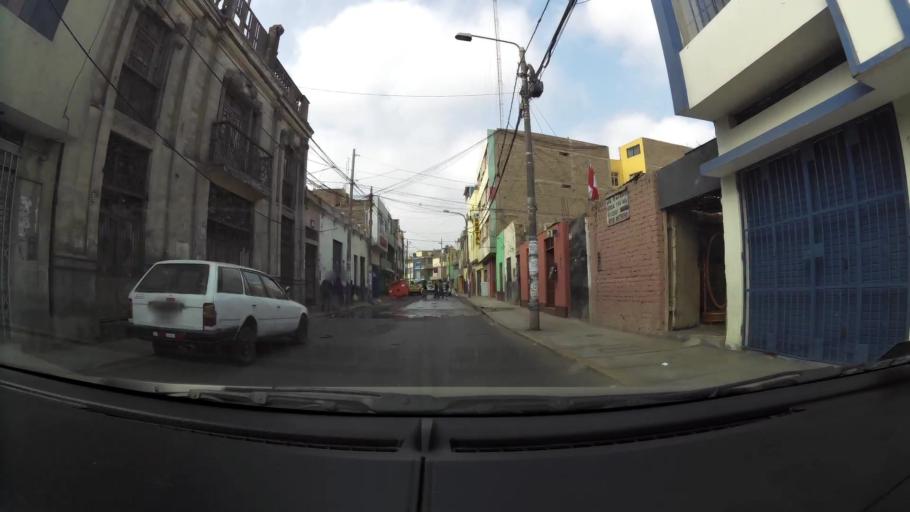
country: PE
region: La Libertad
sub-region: Provincia de Trujillo
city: Trujillo
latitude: -8.1069
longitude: -79.0199
